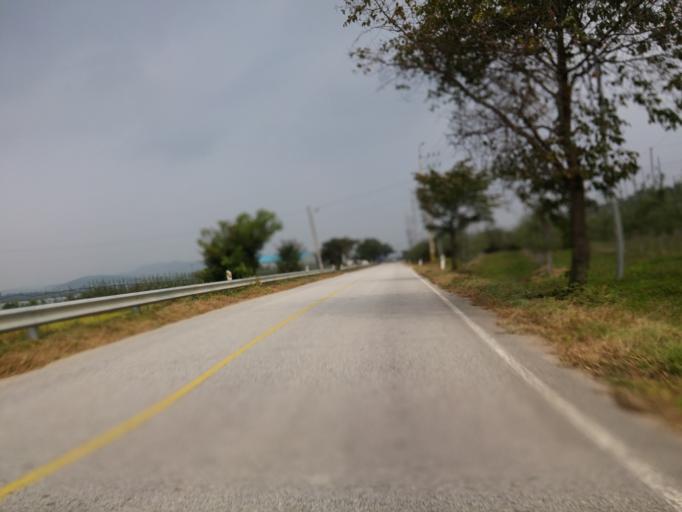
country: KR
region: Chungcheongbuk-do
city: Okcheon
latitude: 36.4045
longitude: 127.7484
